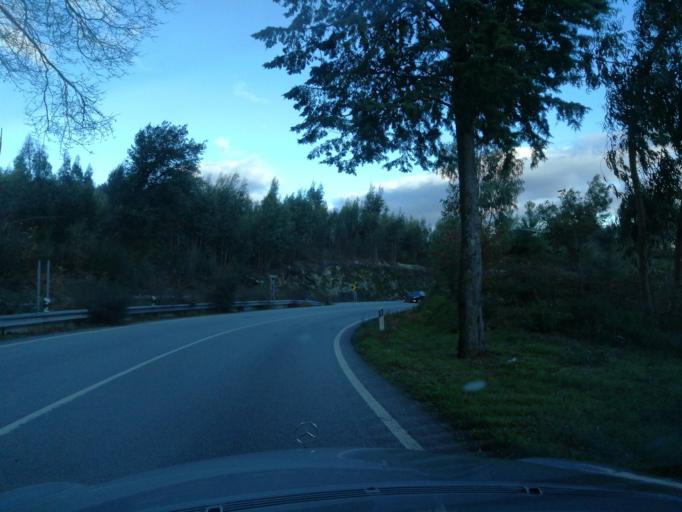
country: PT
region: Braga
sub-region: Barcelos
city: Vila Frescainha
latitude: 41.5686
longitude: -8.6764
